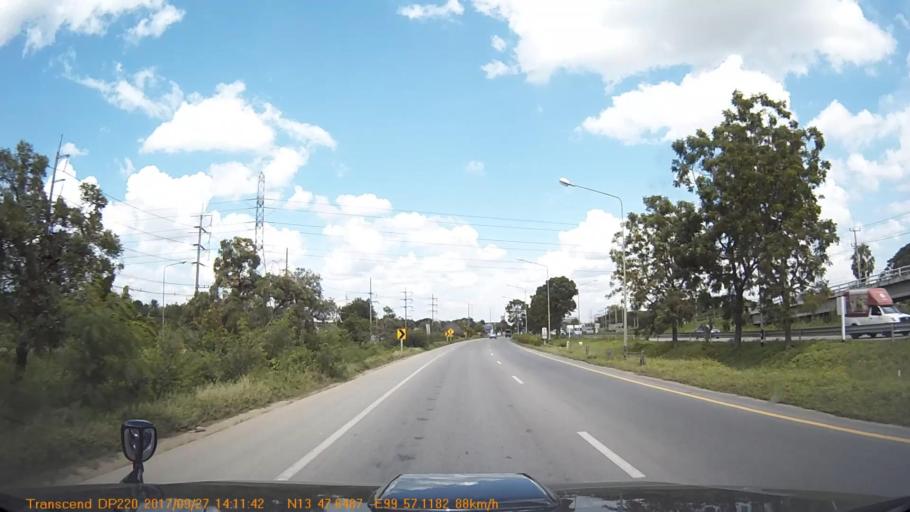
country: TH
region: Ratchaburi
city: Ban Pong
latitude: 13.7941
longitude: 99.9519
